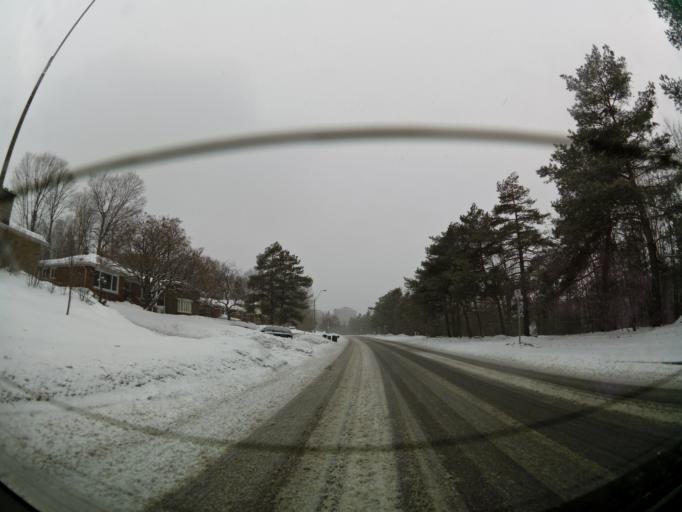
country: CA
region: Ontario
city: Ottawa
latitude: 45.4107
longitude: -75.6487
